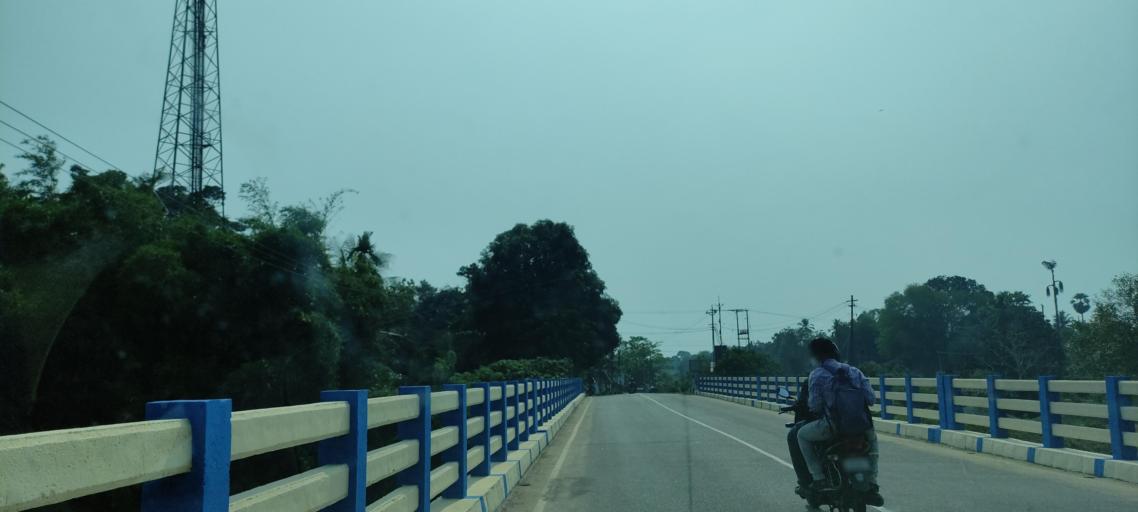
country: IN
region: Kerala
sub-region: Pattanamtitta
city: Tiruvalla
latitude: 9.3493
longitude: 76.5514
